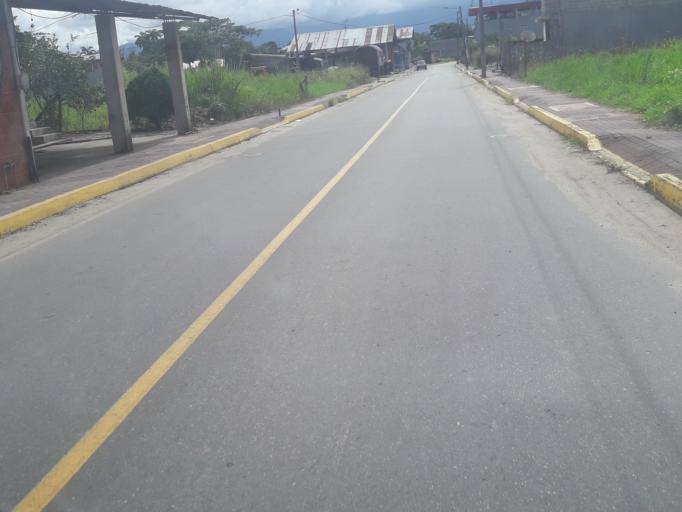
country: EC
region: Napo
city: Tena
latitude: -1.0067
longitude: -77.8165
